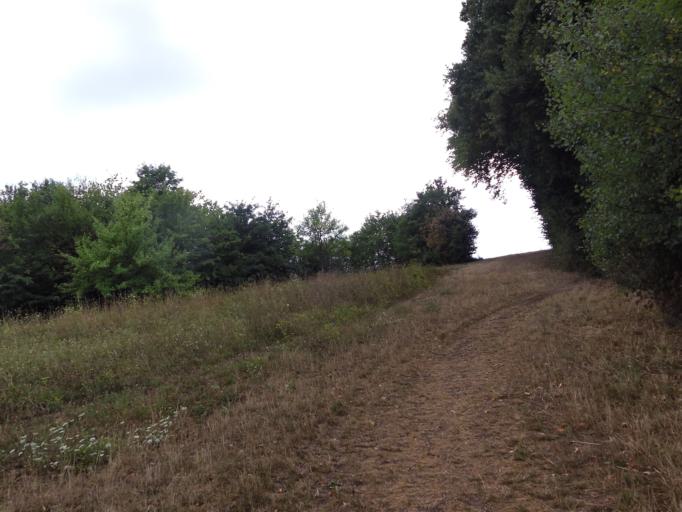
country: DE
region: Bavaria
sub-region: Regierungsbezirk Unterfranken
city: Hochberg
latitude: 49.7791
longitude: 9.8640
